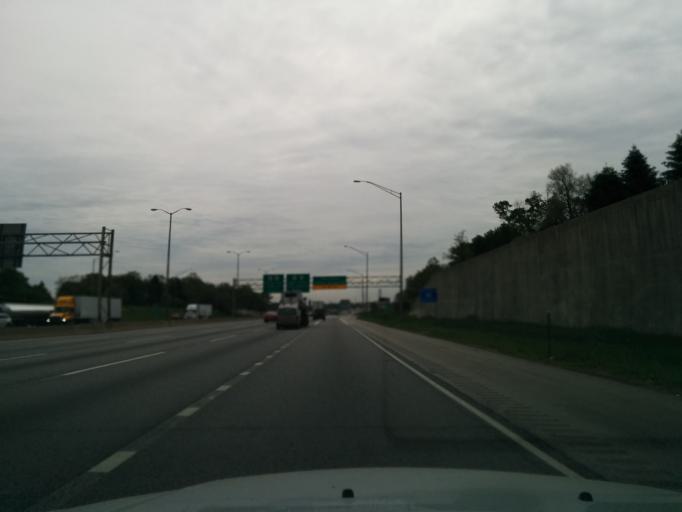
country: US
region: Illinois
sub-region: Cook County
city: Indian Head Park
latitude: 41.7574
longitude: -87.8827
